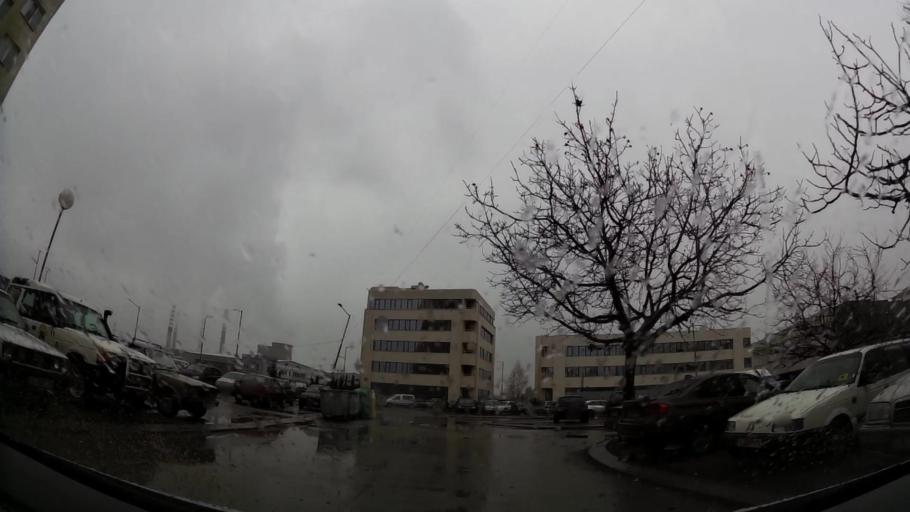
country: BG
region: Sofia-Capital
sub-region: Stolichna Obshtina
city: Sofia
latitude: 42.6481
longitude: 23.4087
